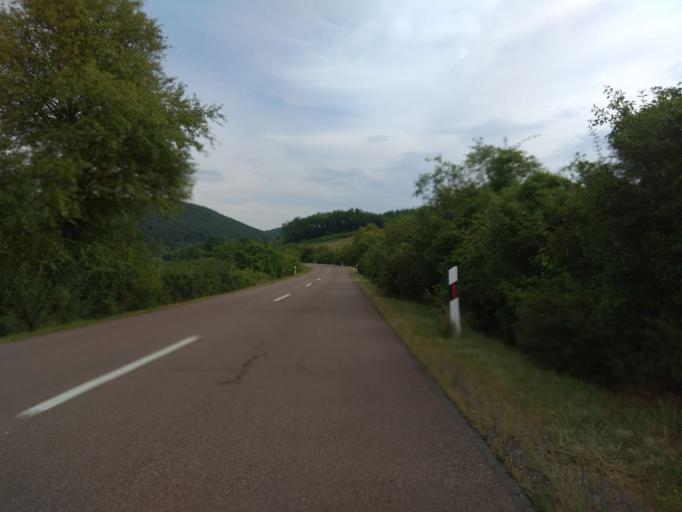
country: HU
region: Heves
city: Belapatfalva
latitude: 48.0230
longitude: 20.2918
